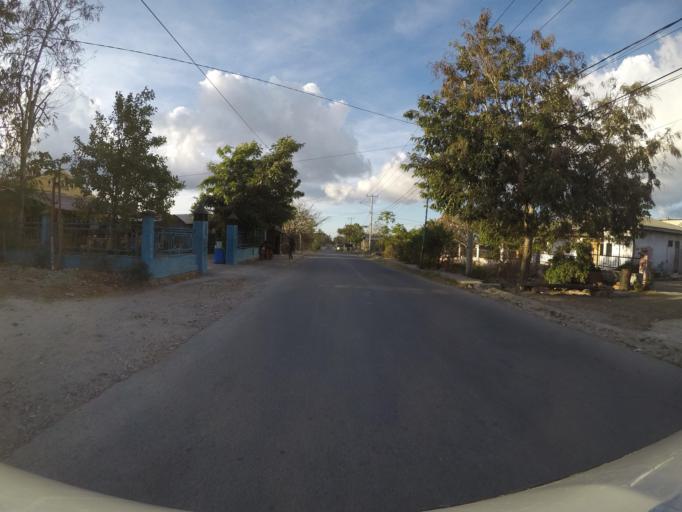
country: TL
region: Baucau
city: Baucau
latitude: -8.4739
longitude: 126.4560
